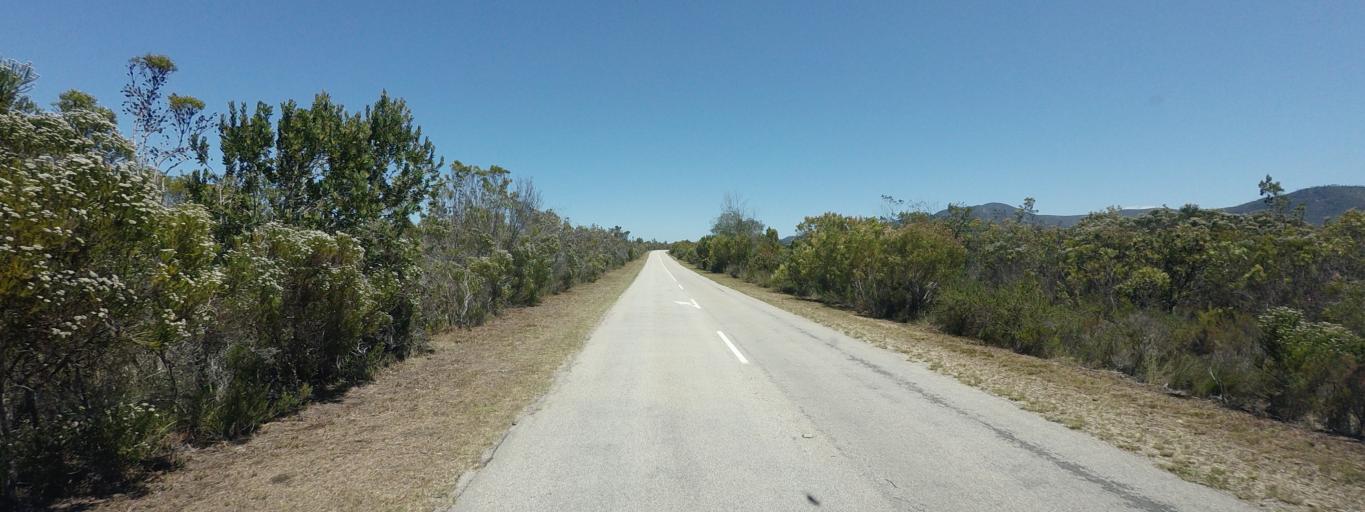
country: ZA
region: Western Cape
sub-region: Eden District Municipality
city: Plettenberg Bay
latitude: -33.9584
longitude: 23.5200
